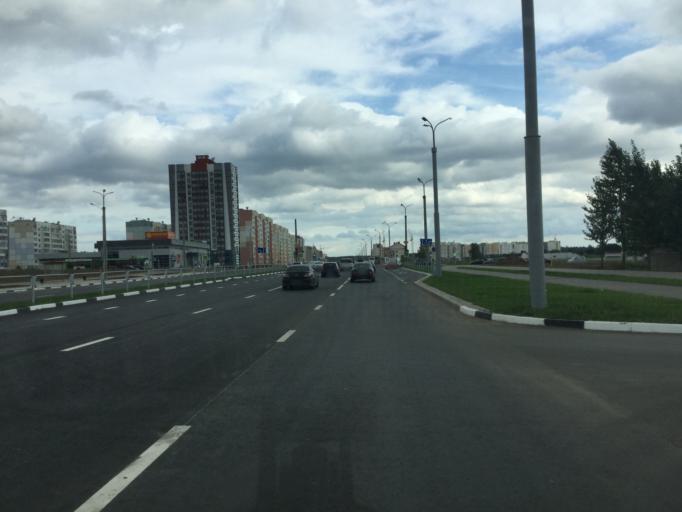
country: BY
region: Vitebsk
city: Vitebsk
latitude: 55.1665
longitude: 30.2530
